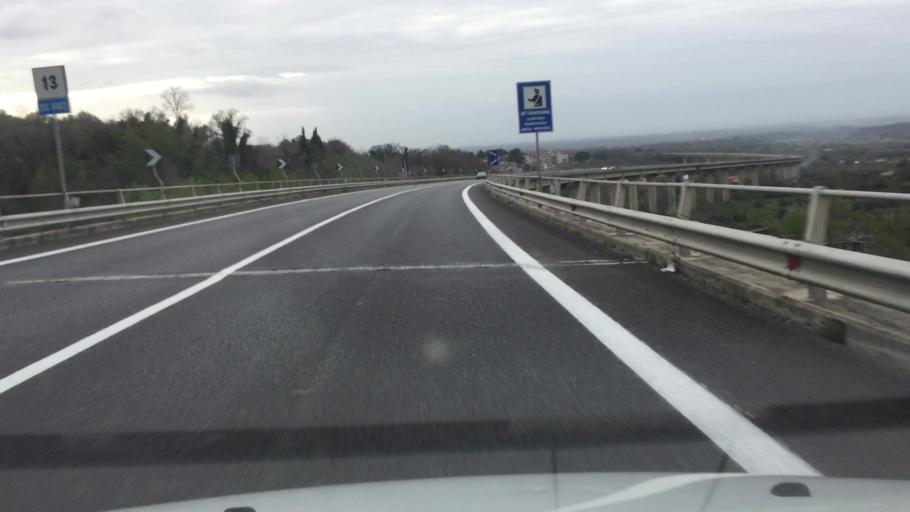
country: IT
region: Calabria
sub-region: Provincia di Reggio Calabria
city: Anoia Superiore
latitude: 38.4167
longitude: 16.1082
